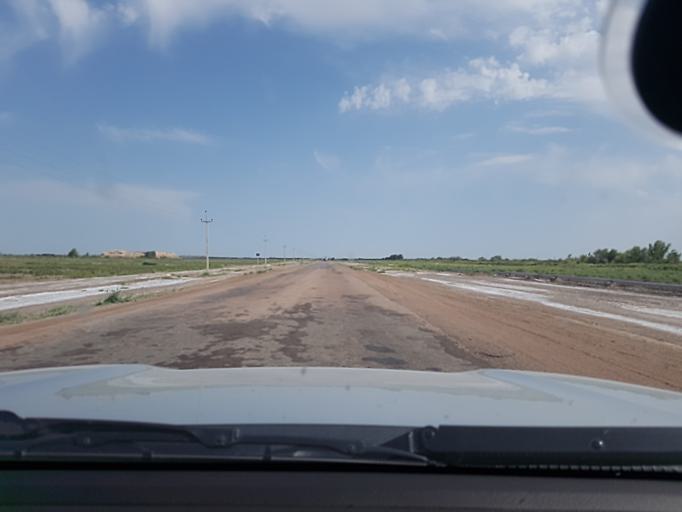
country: TM
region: Dasoguz
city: Boldumsaz
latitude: 42.0617
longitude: 59.7676
